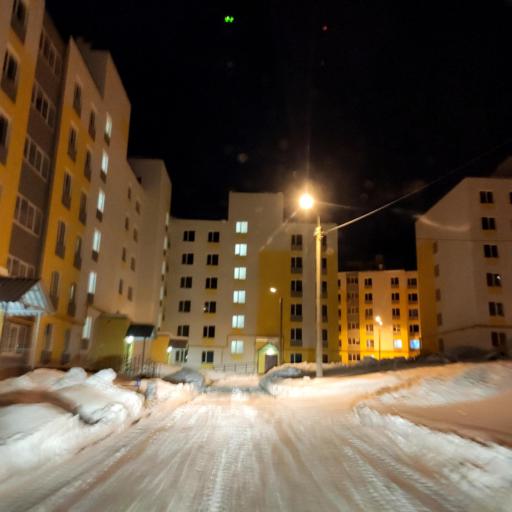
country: RU
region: Bashkortostan
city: Mikhaylovka
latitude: 54.7547
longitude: 55.7912
